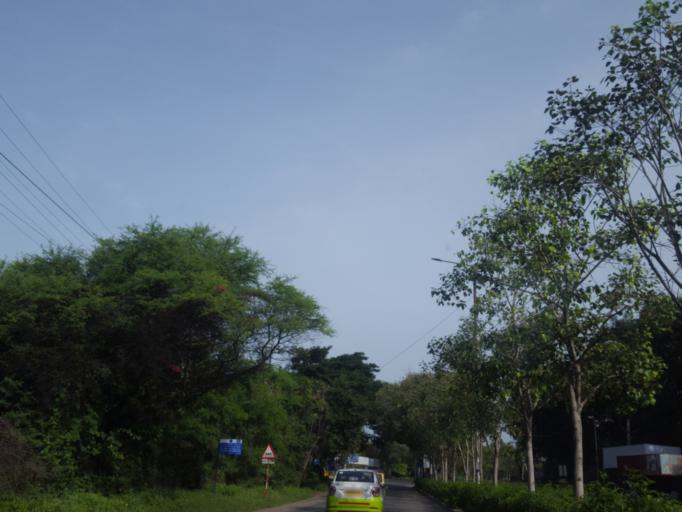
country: IN
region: Telangana
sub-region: Medak
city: Serilingampalle
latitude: 17.4610
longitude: 78.3365
